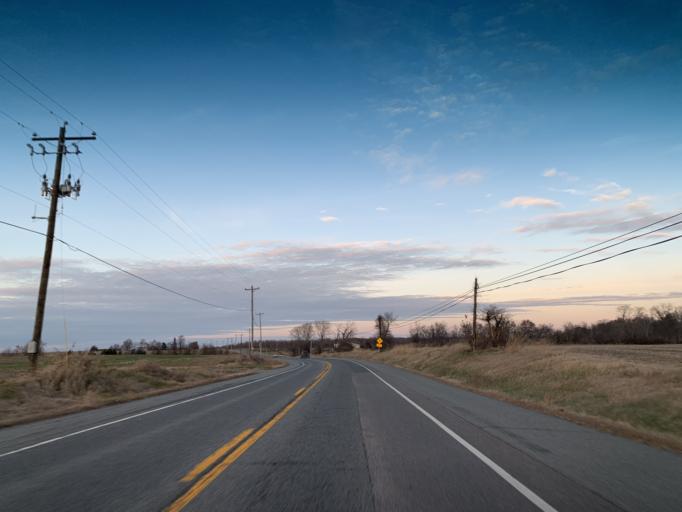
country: US
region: Delaware
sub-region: New Castle County
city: Middletown
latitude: 39.4151
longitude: -75.8619
